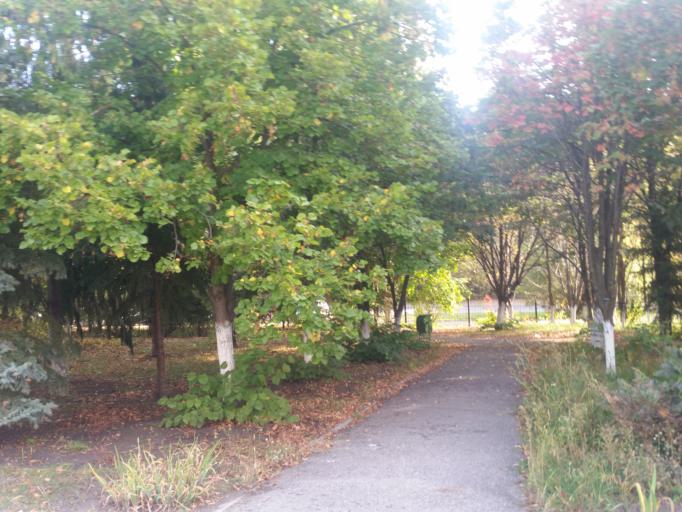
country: RU
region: Ulyanovsk
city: Dimitrovgrad
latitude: 54.2437
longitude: 49.5985
